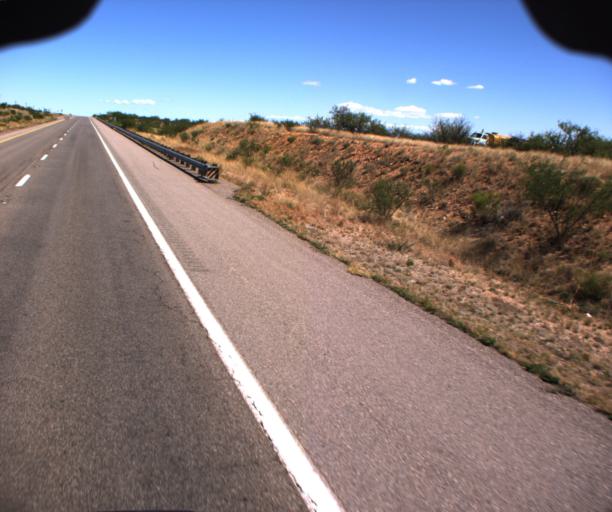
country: US
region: Arizona
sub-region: Cochise County
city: Whetstone
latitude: 31.8553
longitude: -110.3410
